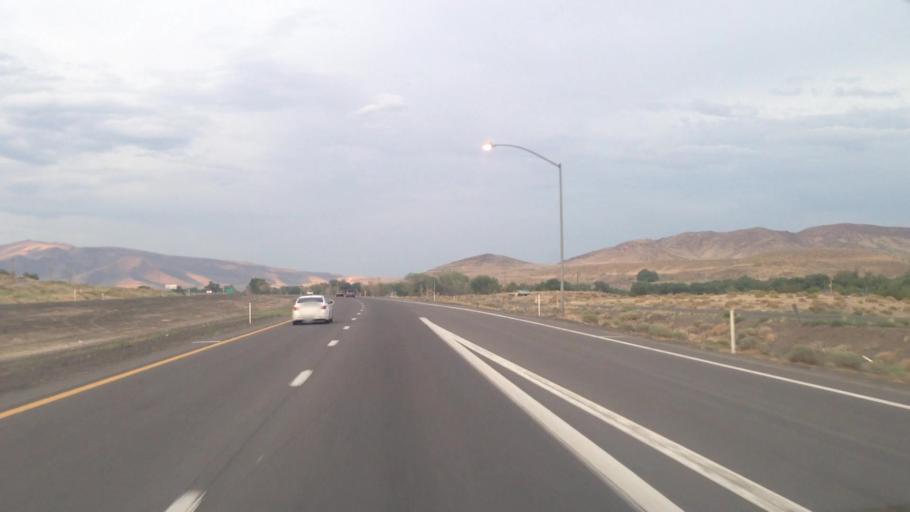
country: US
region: Nevada
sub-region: Lyon County
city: Fernley
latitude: 39.6044
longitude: -119.3297
